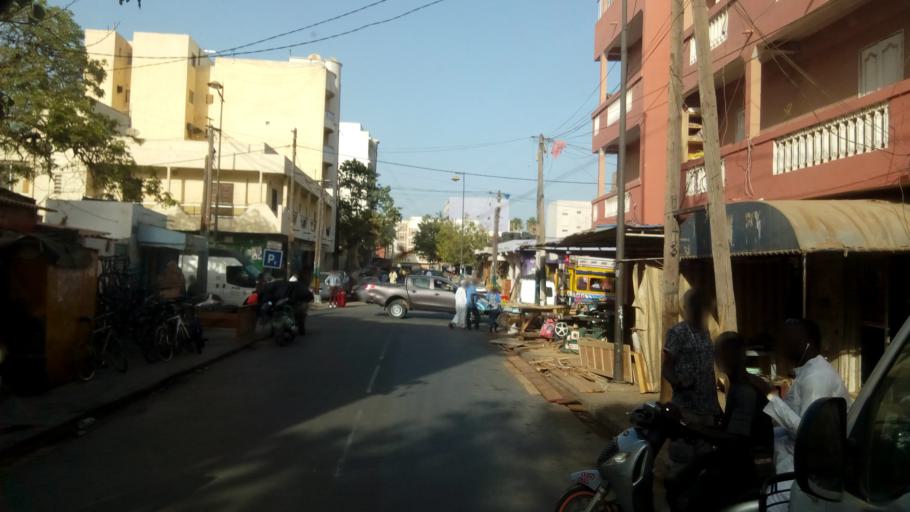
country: SN
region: Dakar
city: Dakar
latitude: 14.6822
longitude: -17.4467
